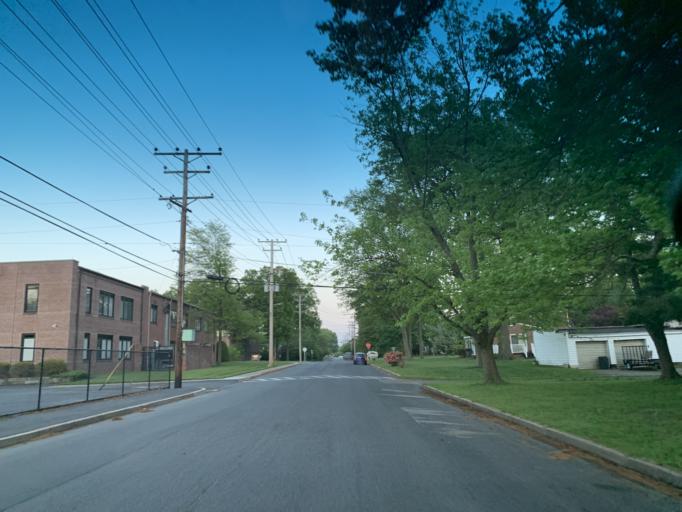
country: US
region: Maryland
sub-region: Harford County
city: Aberdeen
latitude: 39.5073
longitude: -76.1719
